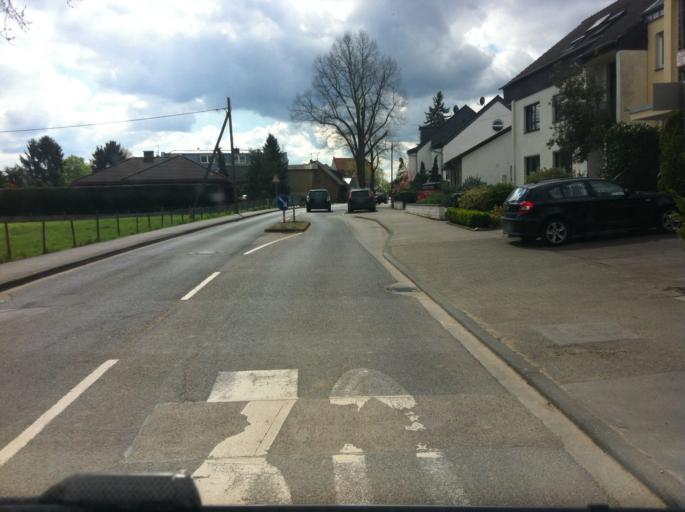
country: DE
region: North Rhine-Westphalia
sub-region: Regierungsbezirk Koln
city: Sinnersdorf
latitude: 51.0167
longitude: 6.8545
